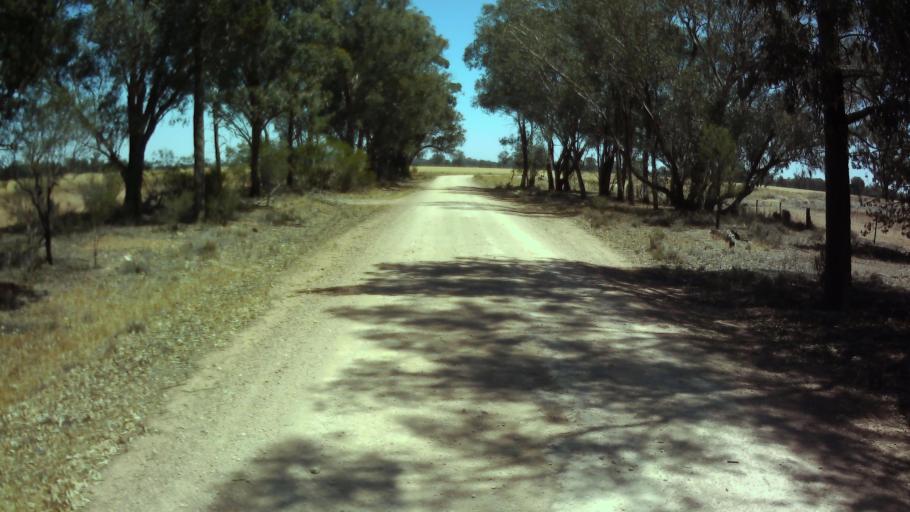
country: AU
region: New South Wales
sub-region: Weddin
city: Grenfell
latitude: -34.0074
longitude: 147.9575
